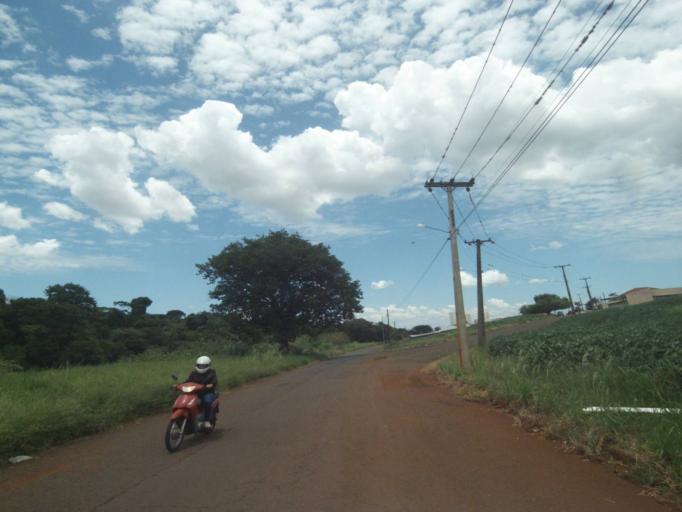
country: BR
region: Parana
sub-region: Londrina
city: Londrina
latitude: -23.3185
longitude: -51.2075
